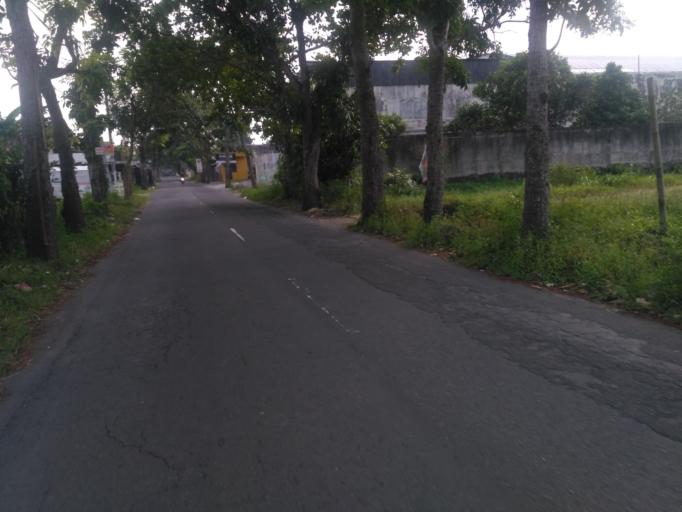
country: ID
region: Daerah Istimewa Yogyakarta
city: Yogyakarta
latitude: -7.7751
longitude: 110.3420
